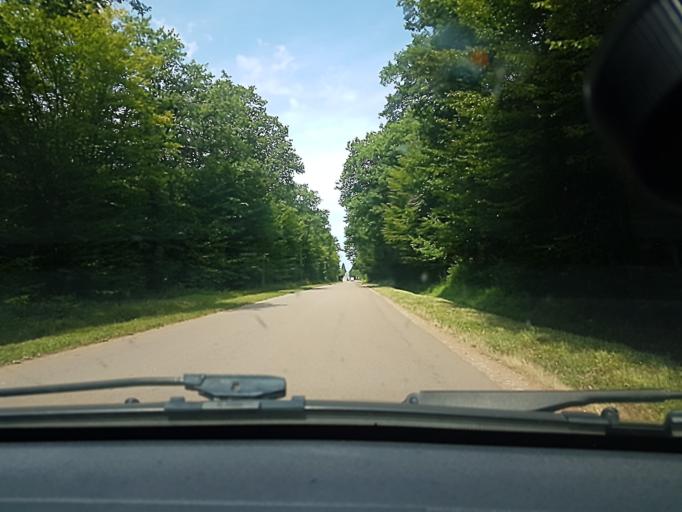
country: FR
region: Bourgogne
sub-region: Departement de Saone-et-Loire
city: Chagny
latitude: 46.8921
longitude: 4.7906
